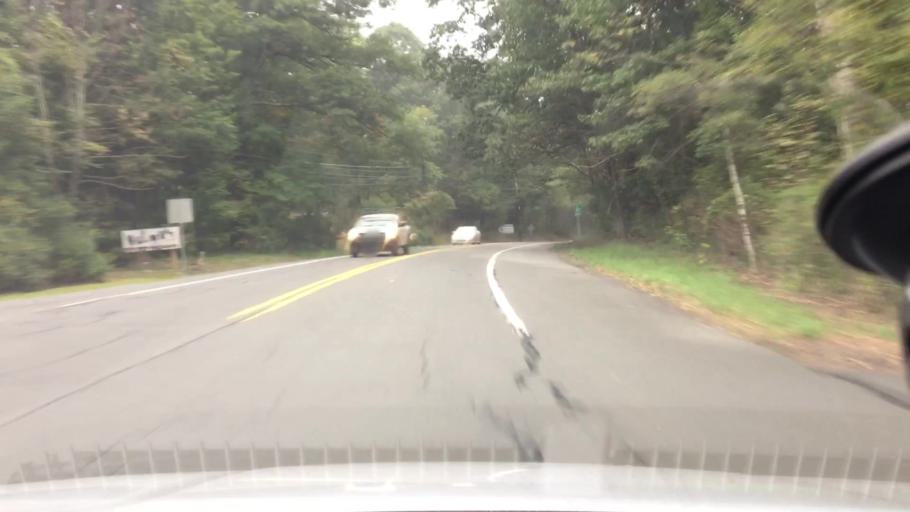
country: US
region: Pennsylvania
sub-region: Monroe County
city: Mountainhome
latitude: 41.1556
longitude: -75.2827
